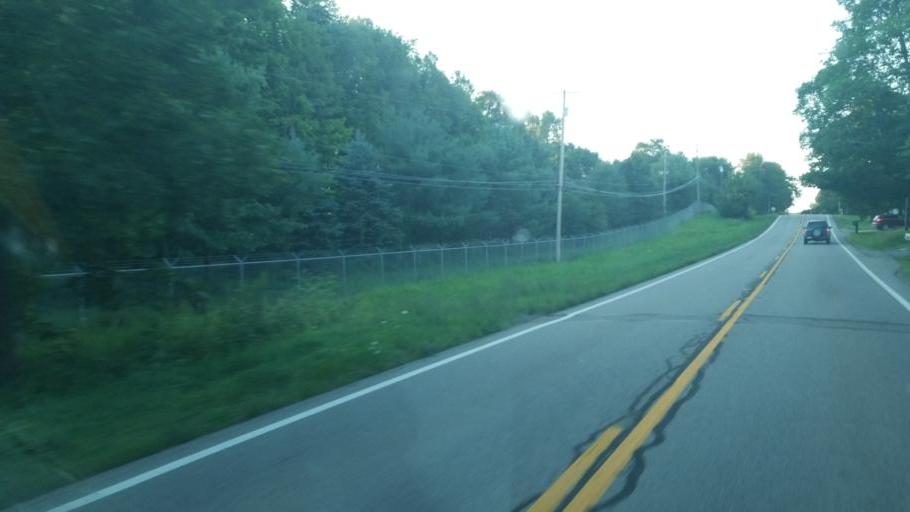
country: US
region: Ohio
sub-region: Trumbull County
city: Newton Falls
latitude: 41.2192
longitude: -80.9797
